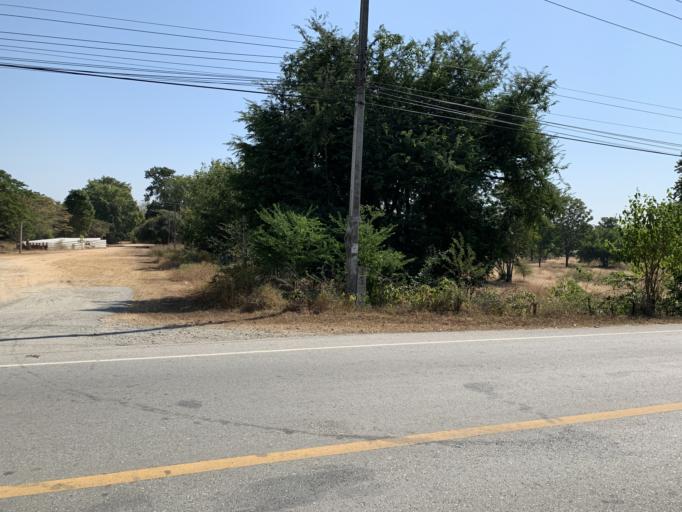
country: TH
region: Tak
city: Sam Ngao
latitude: 17.2413
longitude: 99.0251
